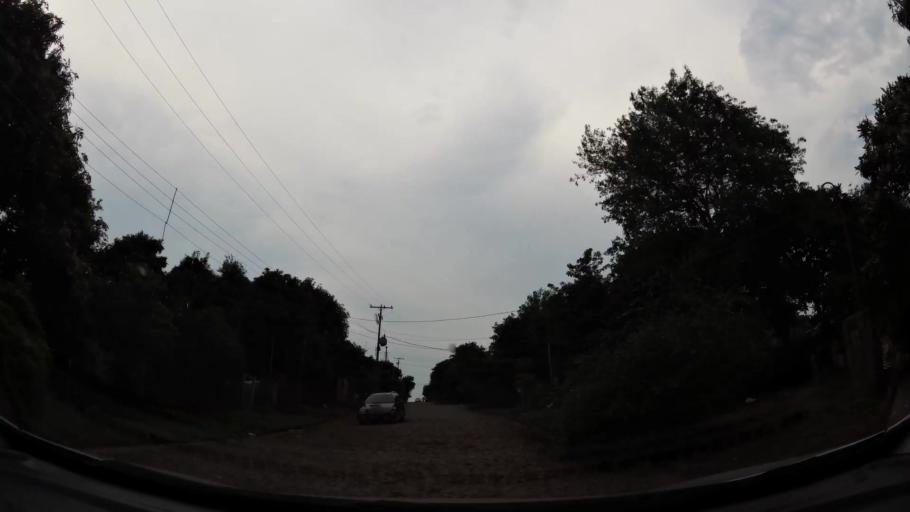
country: BR
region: Parana
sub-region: Foz Do Iguacu
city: Foz do Iguacu
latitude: -25.5489
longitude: -54.5995
